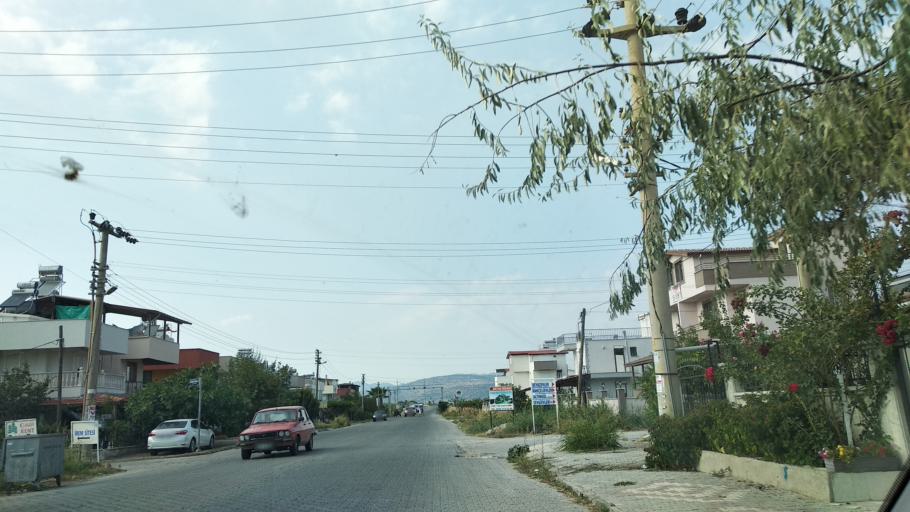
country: TR
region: Izmir
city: Dikili
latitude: 39.1019
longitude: 26.8828
